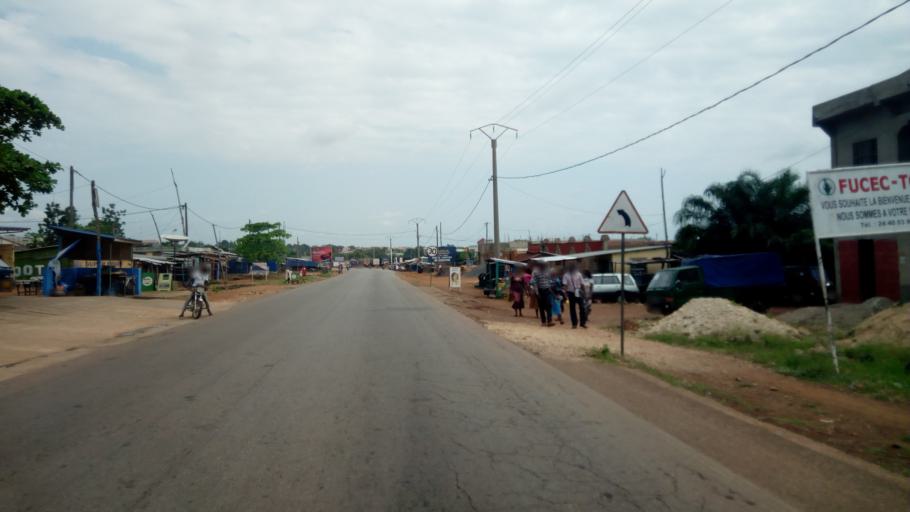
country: TG
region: Plateaux
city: Atakpame
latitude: 7.5017
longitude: 1.1561
